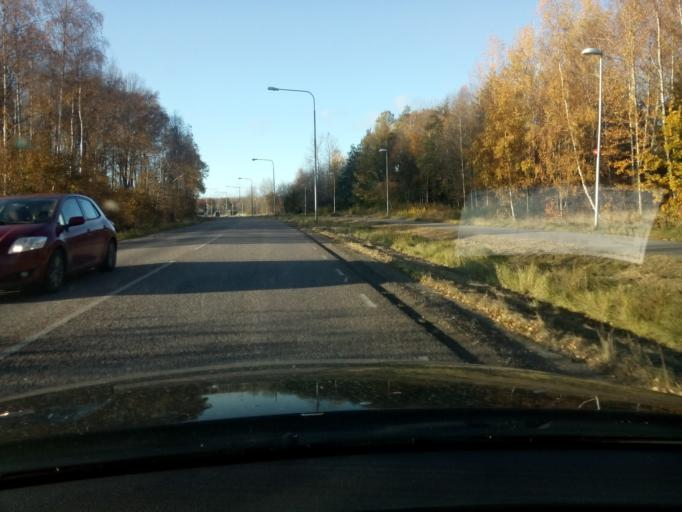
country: SE
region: Soedermanland
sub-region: Nykopings Kommun
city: Nykoping
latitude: 58.7245
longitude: 17.0195
